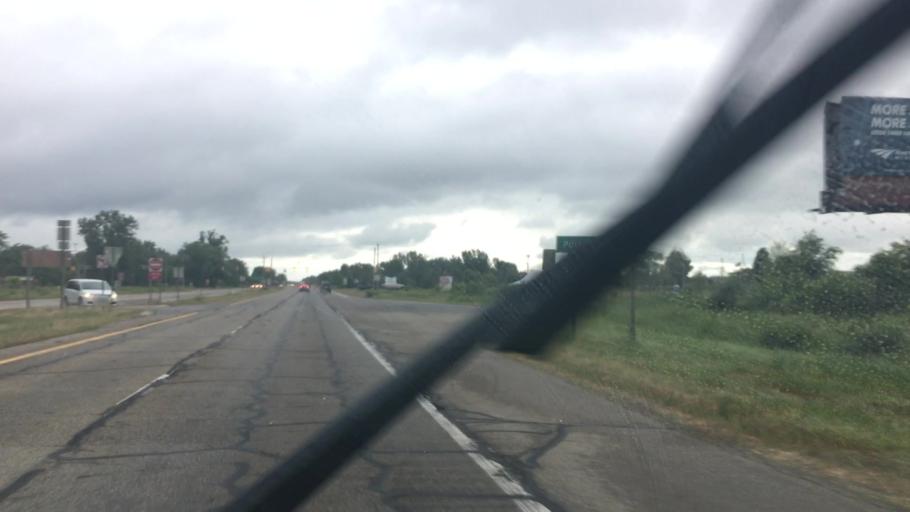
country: US
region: Michigan
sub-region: Ottawa County
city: Beechwood
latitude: 42.8832
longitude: -86.1222
